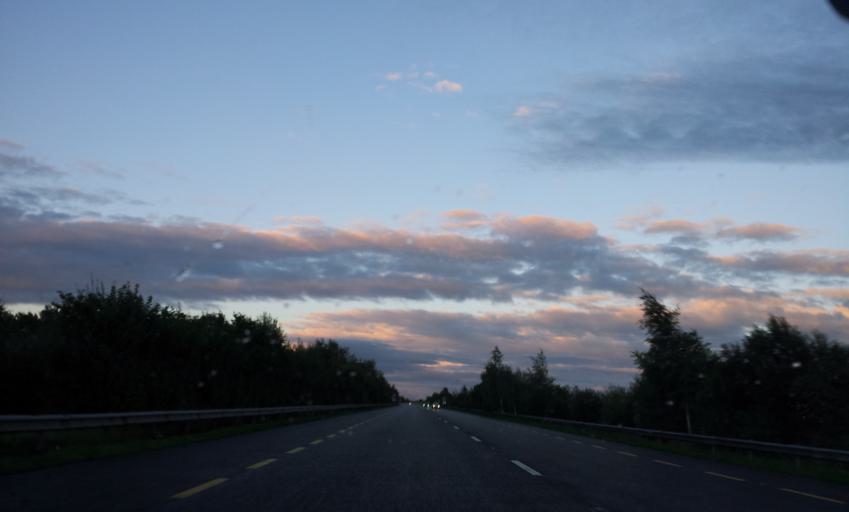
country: IE
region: Munster
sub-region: County Limerick
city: Adare
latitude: 52.5792
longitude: -8.7479
